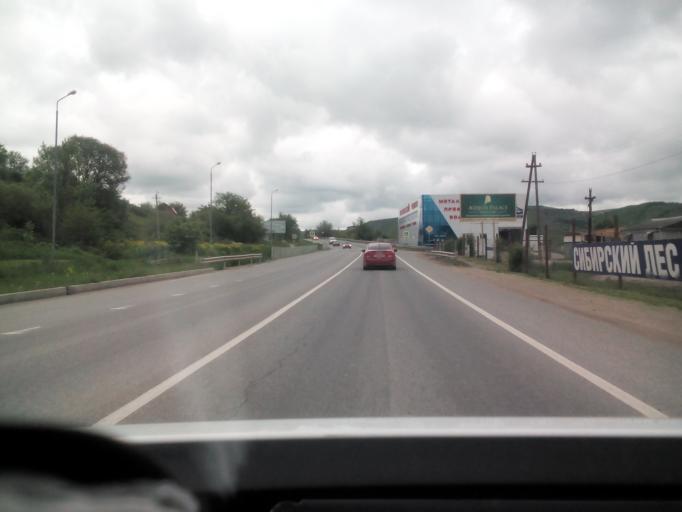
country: RU
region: Stavropol'skiy
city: Yasnaya Polyana
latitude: 43.9644
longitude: 42.7752
